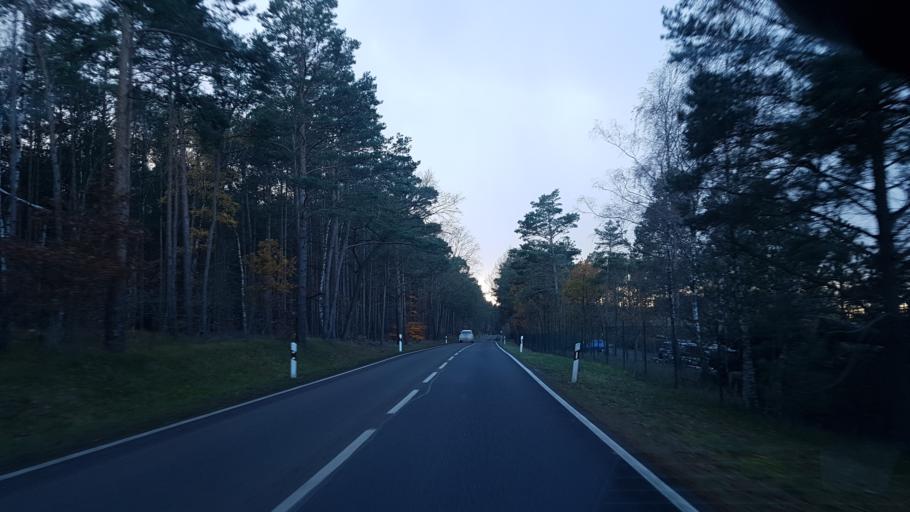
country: DE
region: Brandenburg
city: Sonnewalde
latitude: 51.7263
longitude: 13.6953
